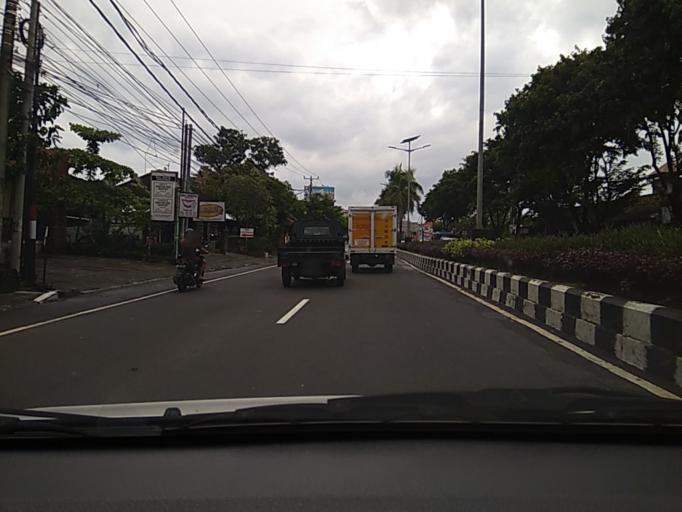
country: ID
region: Bali
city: Jimbaran
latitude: -8.7826
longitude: 115.1814
